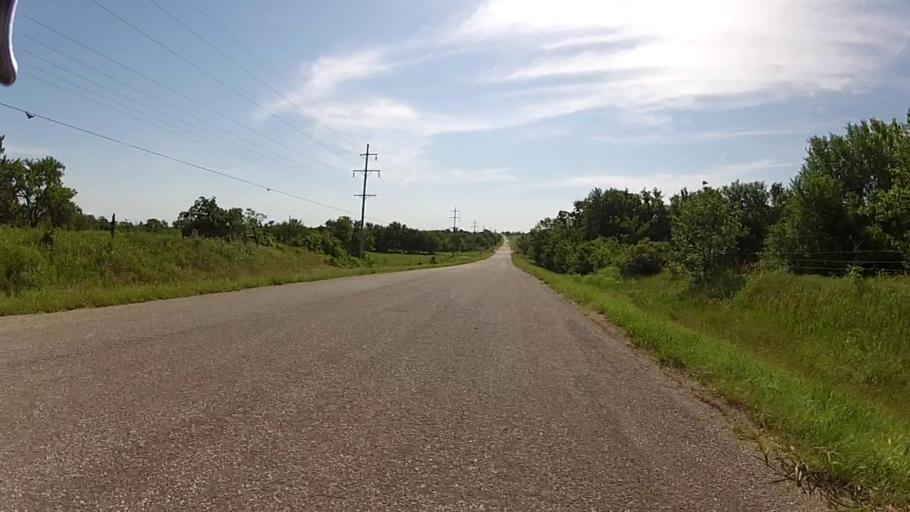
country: US
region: Kansas
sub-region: Cowley County
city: Winfield
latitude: 37.0710
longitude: -96.6681
